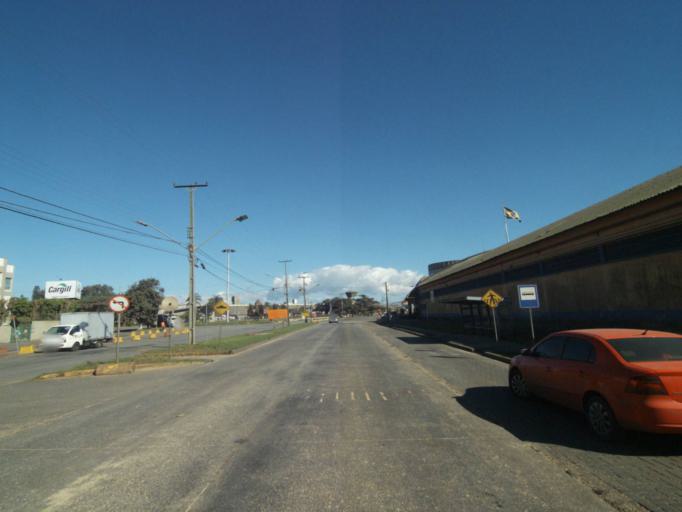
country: BR
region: Parana
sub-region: Paranagua
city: Paranagua
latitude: -25.5039
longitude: -48.5133
